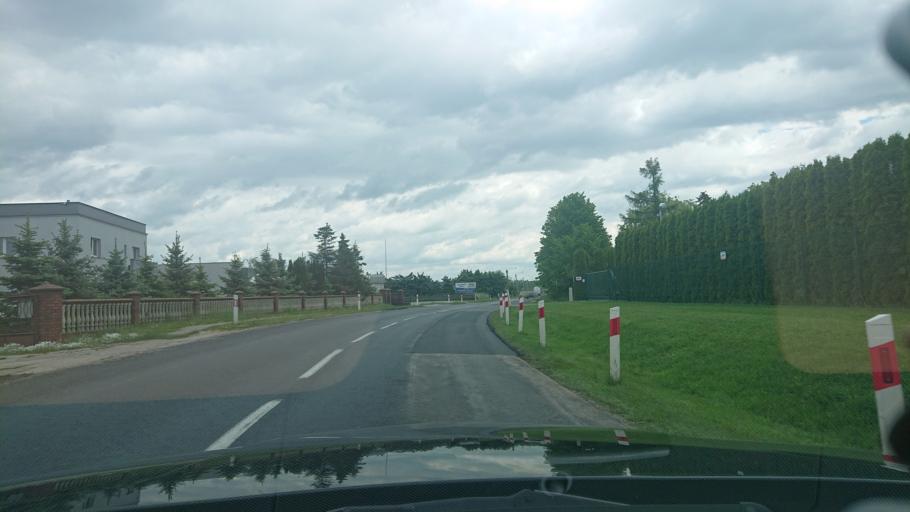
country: PL
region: Greater Poland Voivodeship
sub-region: Powiat gnieznienski
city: Gniezno
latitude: 52.5344
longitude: 17.5451
